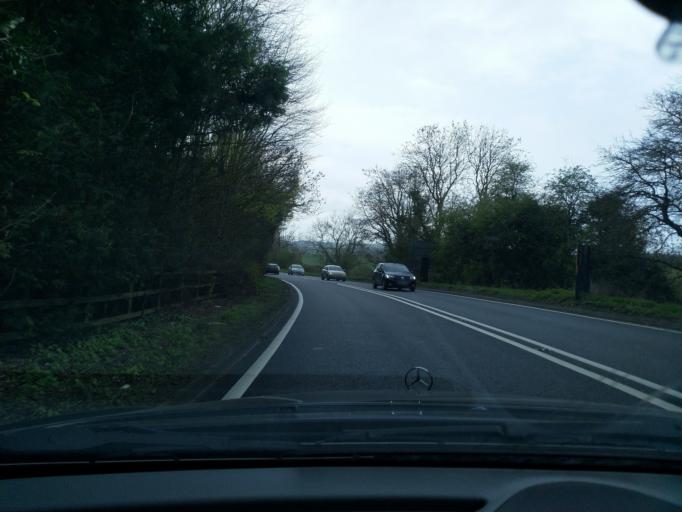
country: GB
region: England
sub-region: Warwickshire
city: Stratford-upon-Avon
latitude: 52.2289
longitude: -1.6625
